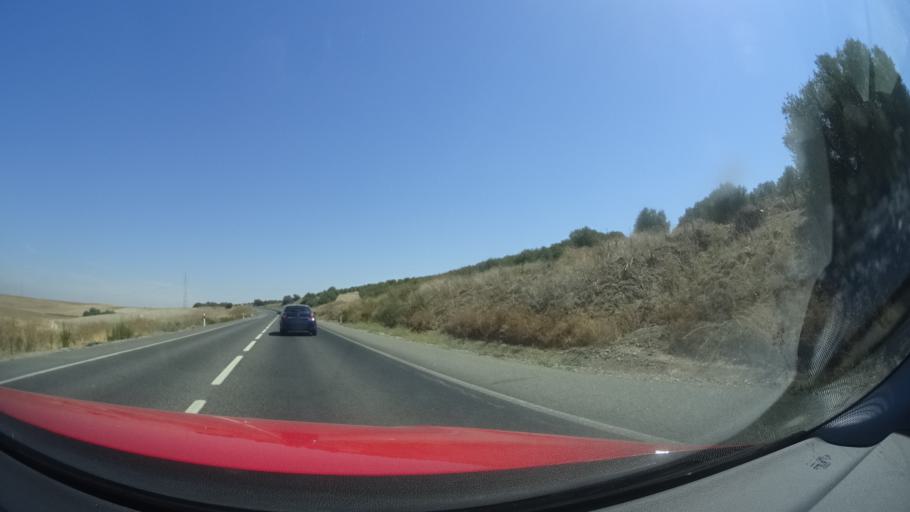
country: ES
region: Andalusia
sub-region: Provincia de Sevilla
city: Las Cabezas de San Juan
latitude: 36.9164
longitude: -5.9475
